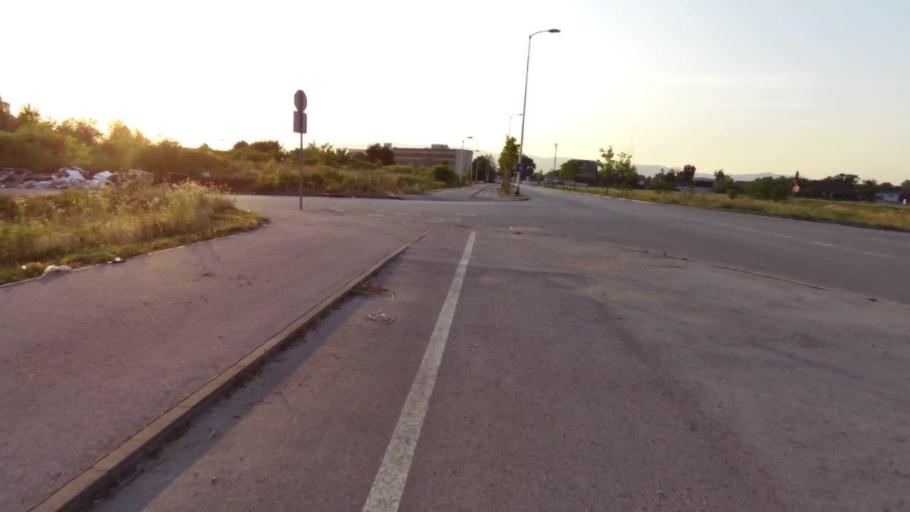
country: HR
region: Grad Zagreb
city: Dubrava
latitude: 45.7988
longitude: 16.0784
